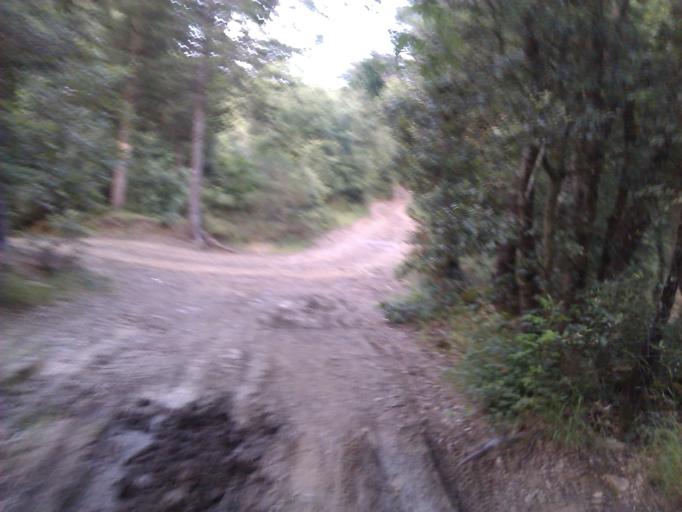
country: IT
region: Tuscany
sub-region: Province of Arezzo
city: Ponticino
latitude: 43.4589
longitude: 11.7414
